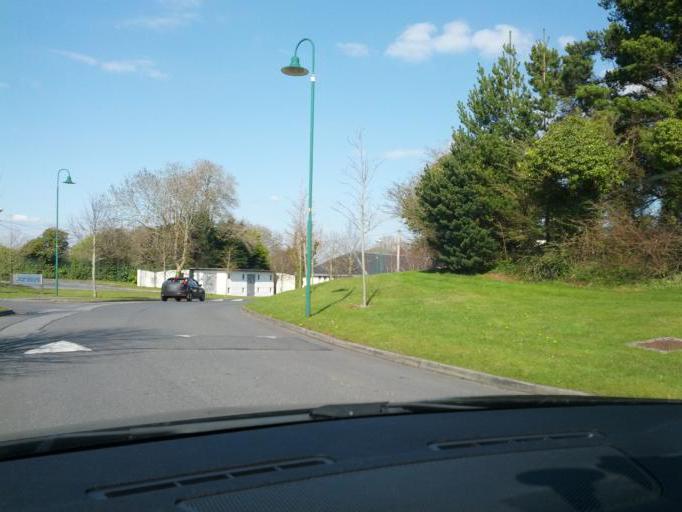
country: IE
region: Connaught
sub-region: County Galway
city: Gaillimh
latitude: 53.2908
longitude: -9.0747
